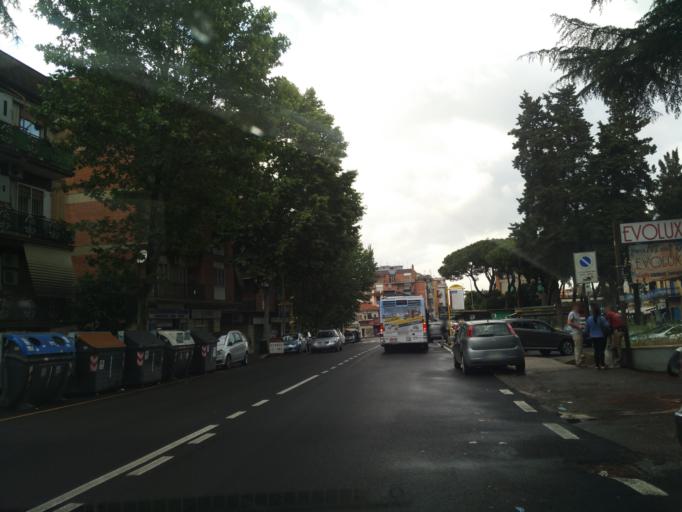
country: IT
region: Latium
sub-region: Citta metropolitana di Roma Capitale
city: Rome
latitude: 41.8803
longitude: 12.5776
